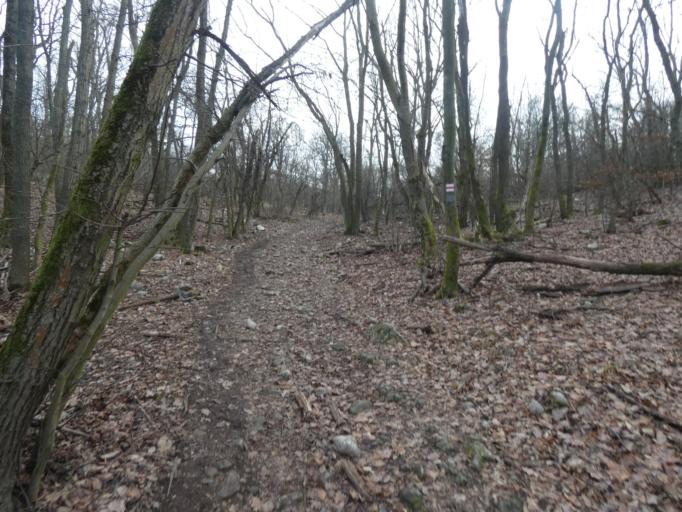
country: HU
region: Pest
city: Solymar
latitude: 47.5566
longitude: 18.9014
